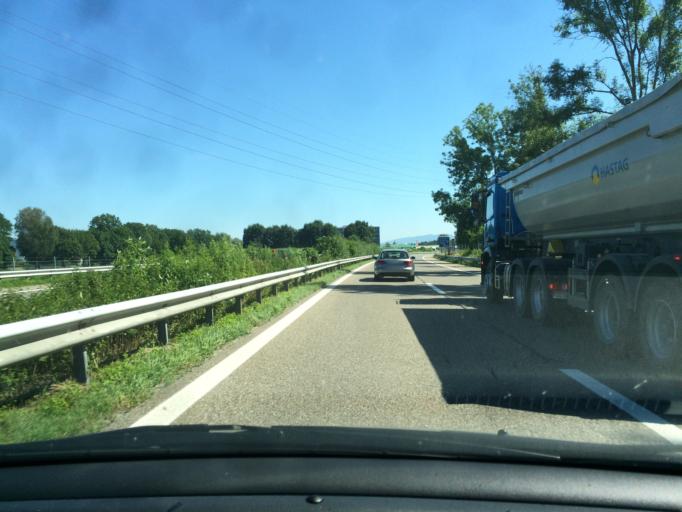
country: AT
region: Vorarlberg
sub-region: Politischer Bezirk Feldkirch
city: Mader
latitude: 47.3547
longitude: 9.6043
